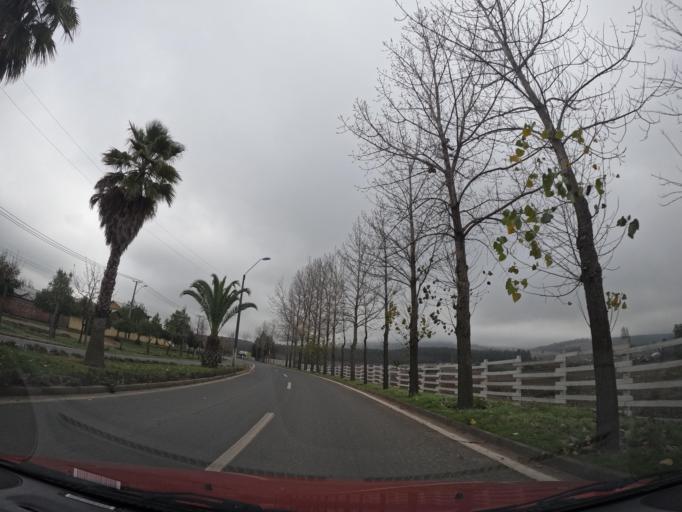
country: CL
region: Maule
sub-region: Provincia de Cauquenes
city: Cauquenes
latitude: -36.2760
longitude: -72.5409
